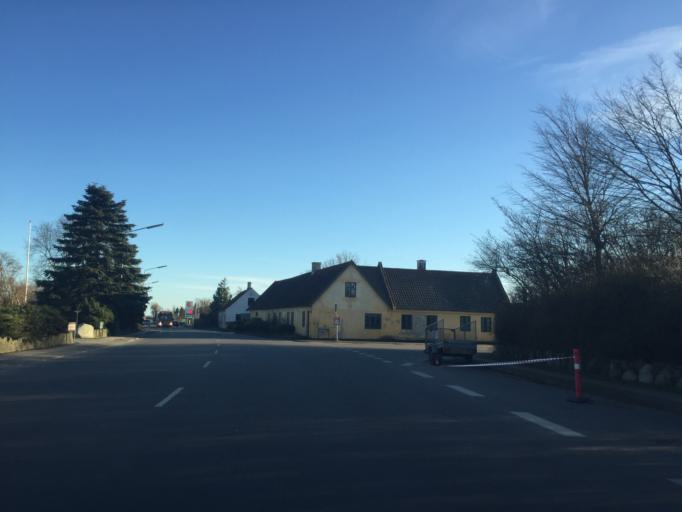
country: DK
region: Capital Region
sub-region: Dragor Kommune
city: Dragor
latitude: 55.5937
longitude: 12.6343
